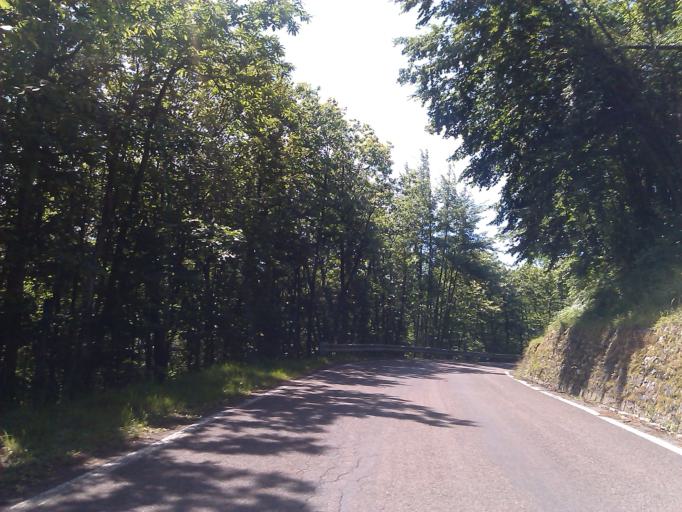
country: IT
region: Tuscany
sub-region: Provincia di Pistoia
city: Sambuca Pistoiese
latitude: 44.1047
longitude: 11.0418
